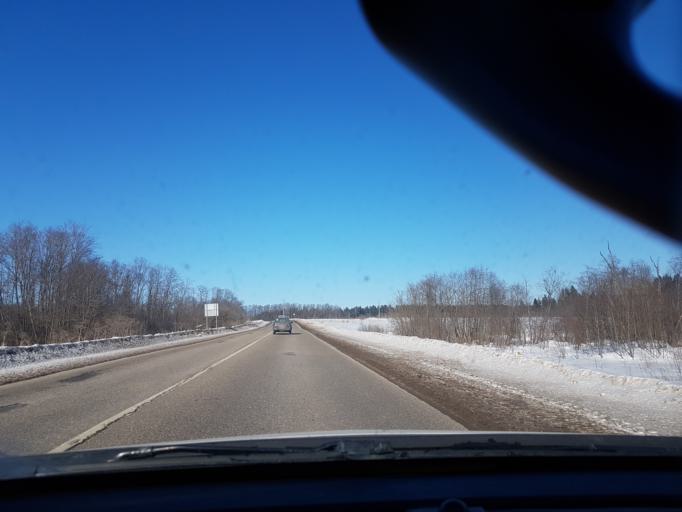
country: RU
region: Moskovskaya
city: Sychevo
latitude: 56.0024
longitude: 36.2363
